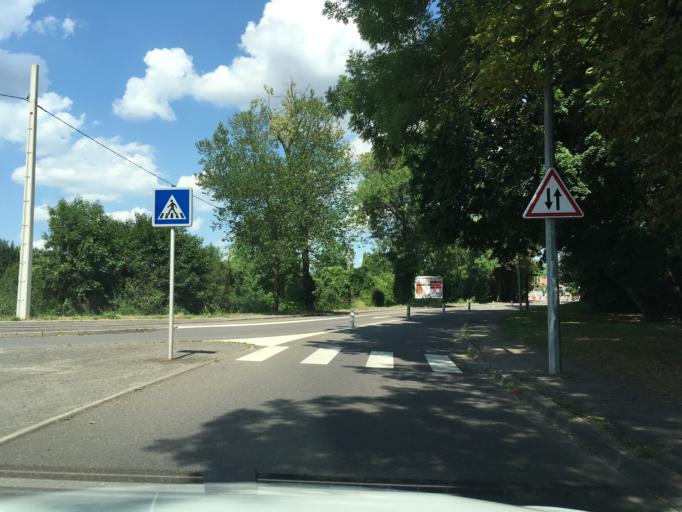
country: FR
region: Lorraine
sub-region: Departement de la Moselle
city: Metz
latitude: 49.1252
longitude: 6.1877
